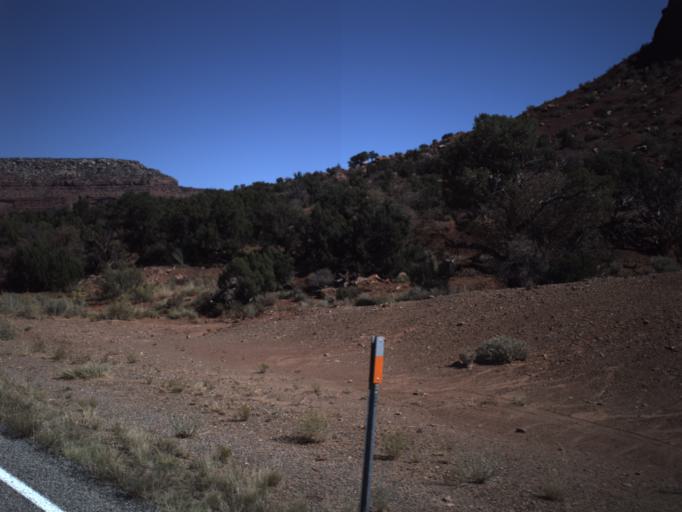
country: US
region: Utah
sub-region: San Juan County
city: Blanding
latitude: 37.6517
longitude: -110.1417
